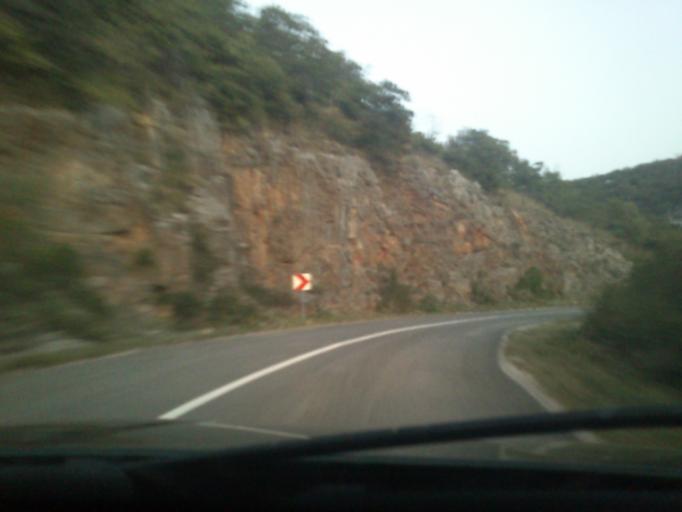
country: HR
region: Licko-Senjska
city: Senj
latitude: 44.9125
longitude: 14.9458
